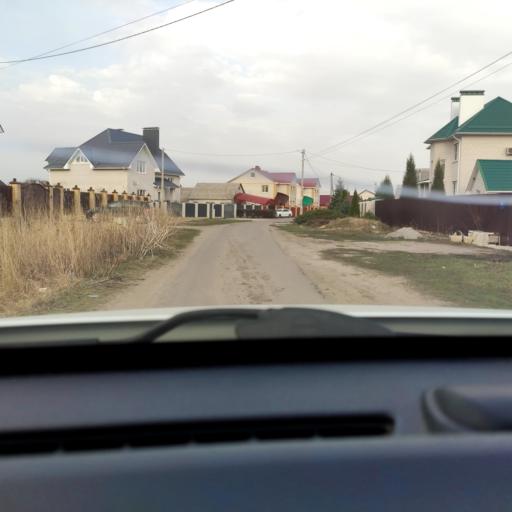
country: RU
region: Voronezj
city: Novaya Usman'
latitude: 51.6648
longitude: 39.3389
